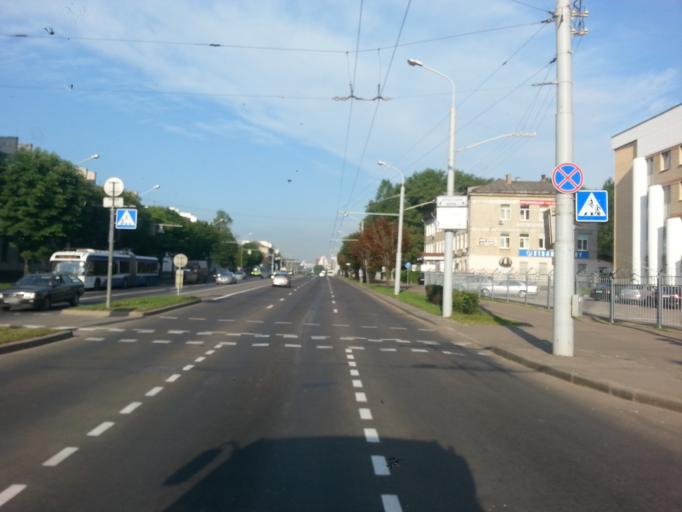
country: BY
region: Minsk
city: Minsk
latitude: 53.9316
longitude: 27.5429
